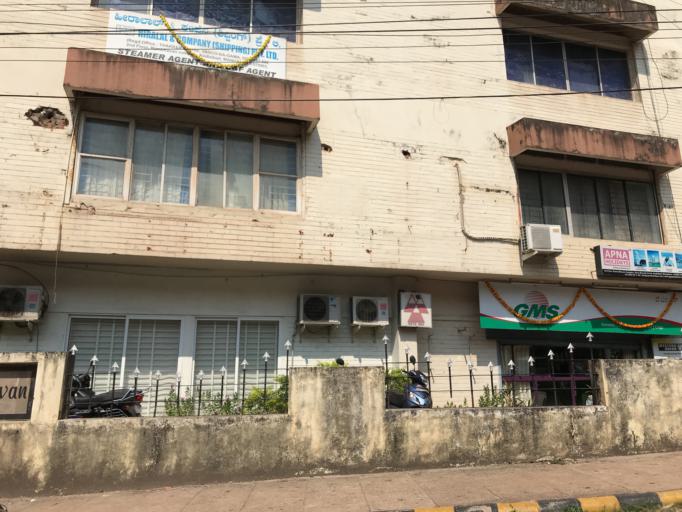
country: IN
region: Karnataka
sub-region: Dakshina Kannada
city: Mangalore
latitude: 12.8741
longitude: 74.8406
